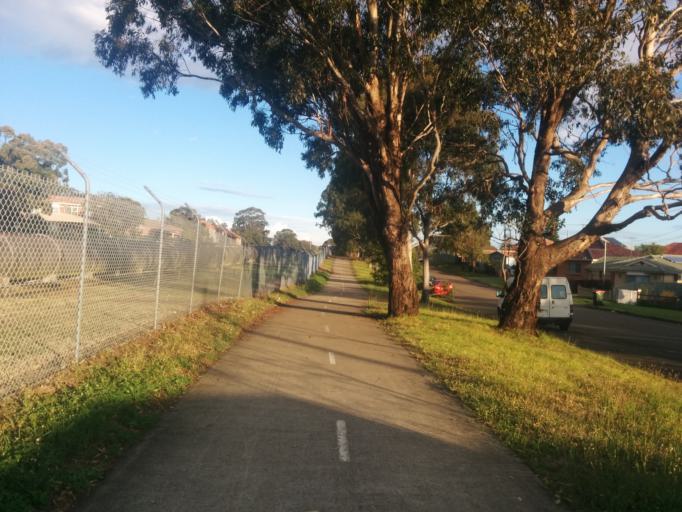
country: AU
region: New South Wales
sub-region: Holroyd
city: Guildford West
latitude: -33.8539
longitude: 150.9783
